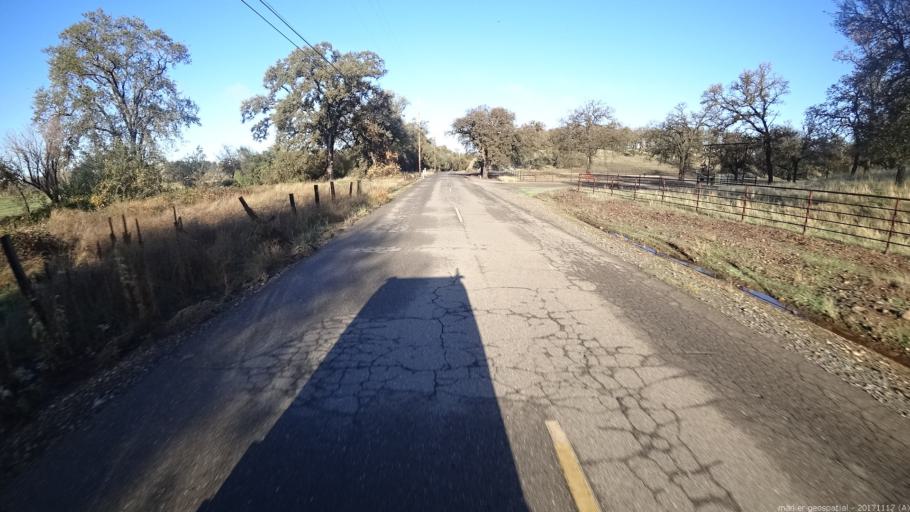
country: US
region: California
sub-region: Shasta County
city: Cottonwood
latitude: 40.4119
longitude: -122.1880
